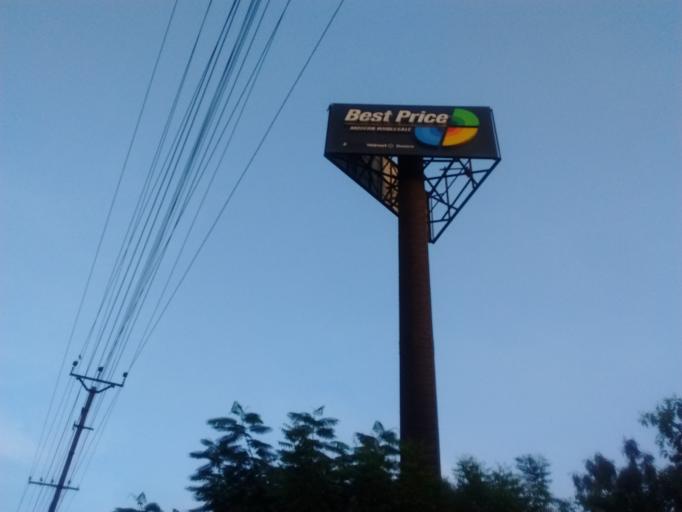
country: IN
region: Andhra Pradesh
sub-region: Krishna
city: Yanamalakuduru
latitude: 16.5114
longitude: 80.7129
